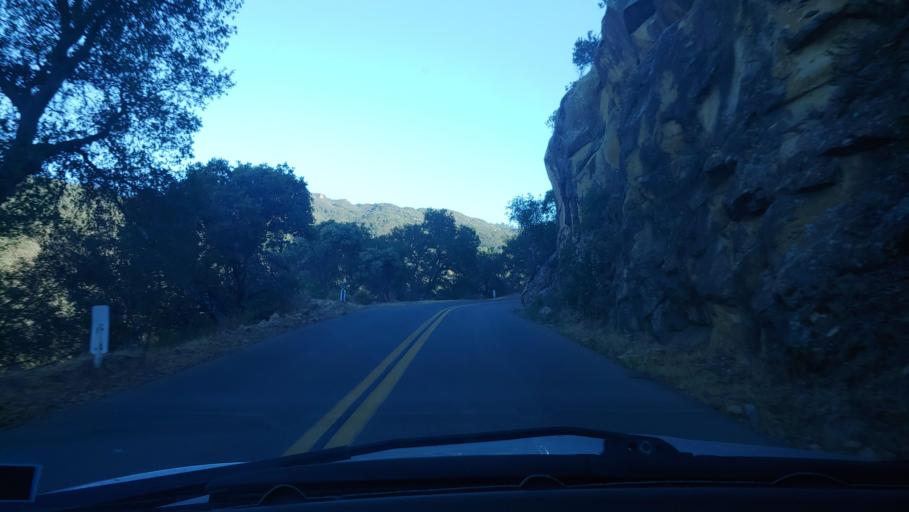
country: US
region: California
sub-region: Santa Barbara County
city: Goleta
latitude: 34.5293
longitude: -119.8342
